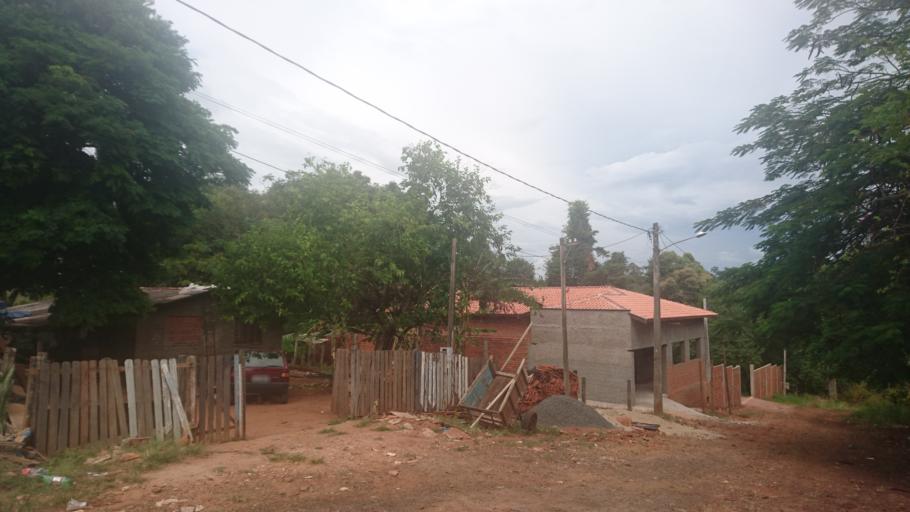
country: BR
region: Sao Paulo
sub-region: Casa Branca
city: Casa Branca
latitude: -21.7848
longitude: -47.0781
